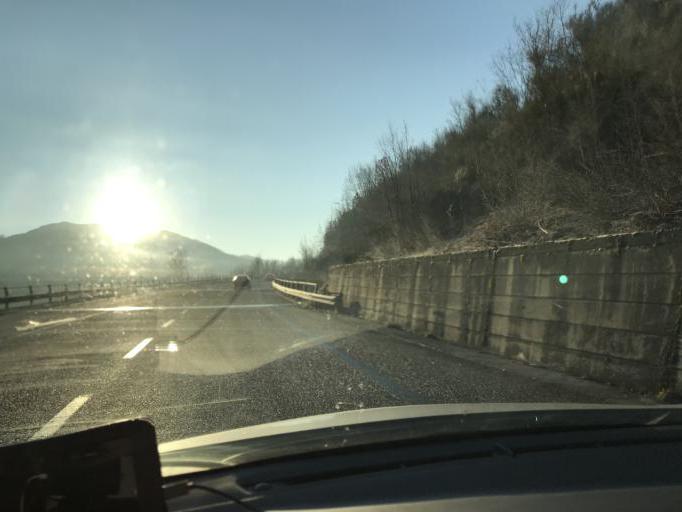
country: IT
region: Latium
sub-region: Provincia di Rieti
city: Concerviano
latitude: 42.3284
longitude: 13.0171
